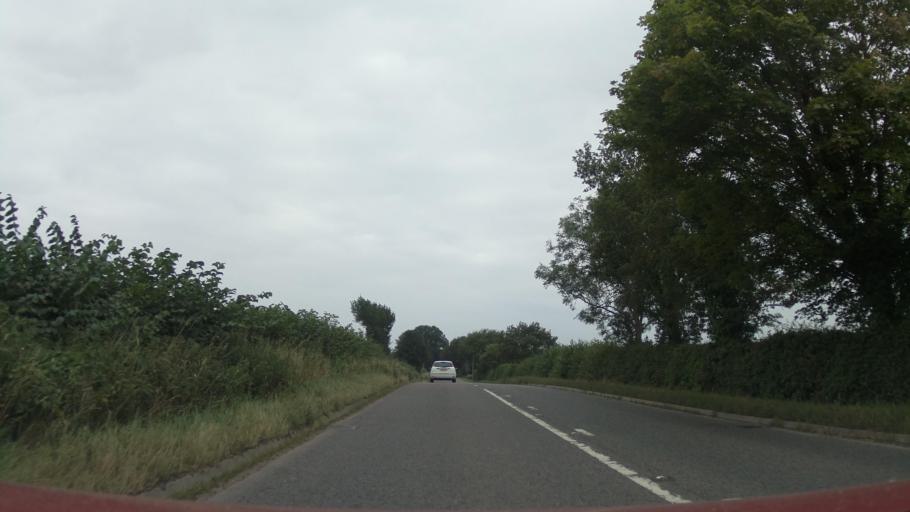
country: GB
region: England
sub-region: Shropshire
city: Shawbury
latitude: 52.8228
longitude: -2.6059
